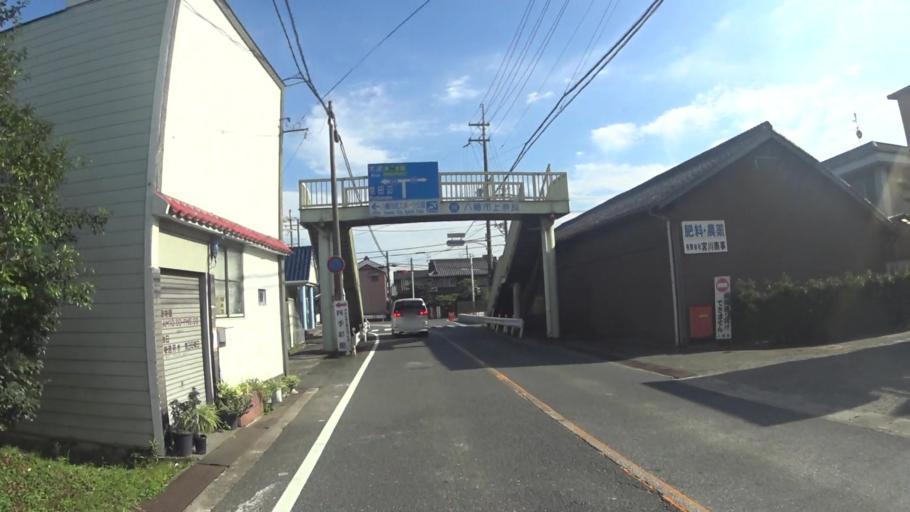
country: JP
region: Kyoto
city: Yawata
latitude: 34.8689
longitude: 135.7312
